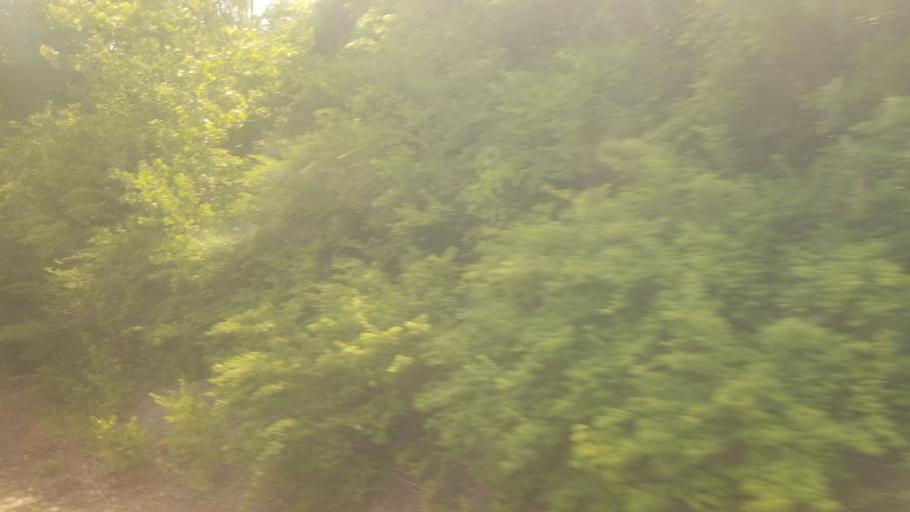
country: US
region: Missouri
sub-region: Jackson County
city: Sugar Creek
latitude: 39.1436
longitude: -94.4189
